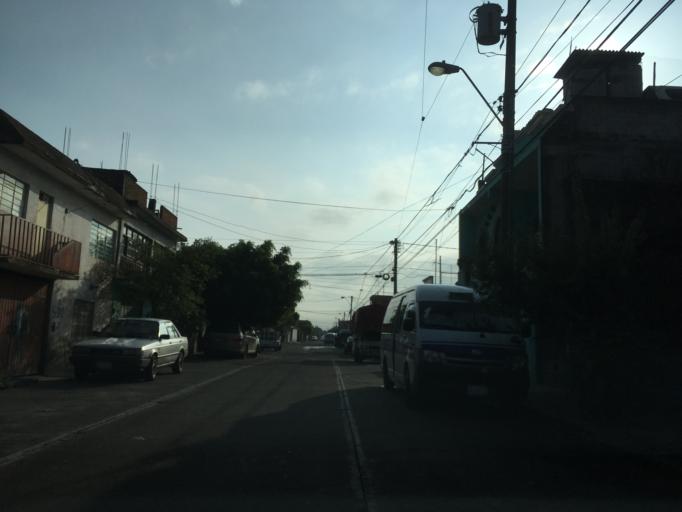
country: MX
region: Michoacan
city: Morelia
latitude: 19.6908
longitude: -101.2228
